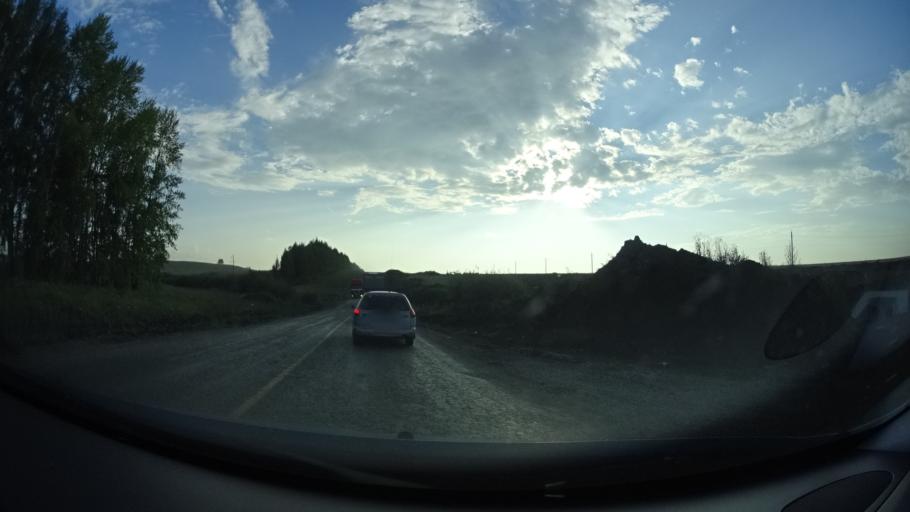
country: RU
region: Samara
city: Kamyshla
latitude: 54.0697
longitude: 52.1819
